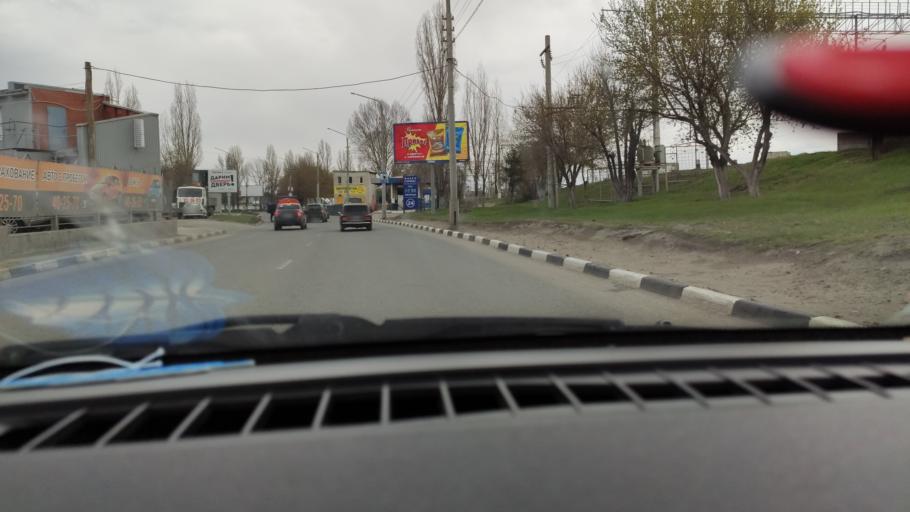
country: RU
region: Saratov
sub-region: Saratovskiy Rayon
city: Saratov
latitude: 51.5799
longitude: 45.9810
